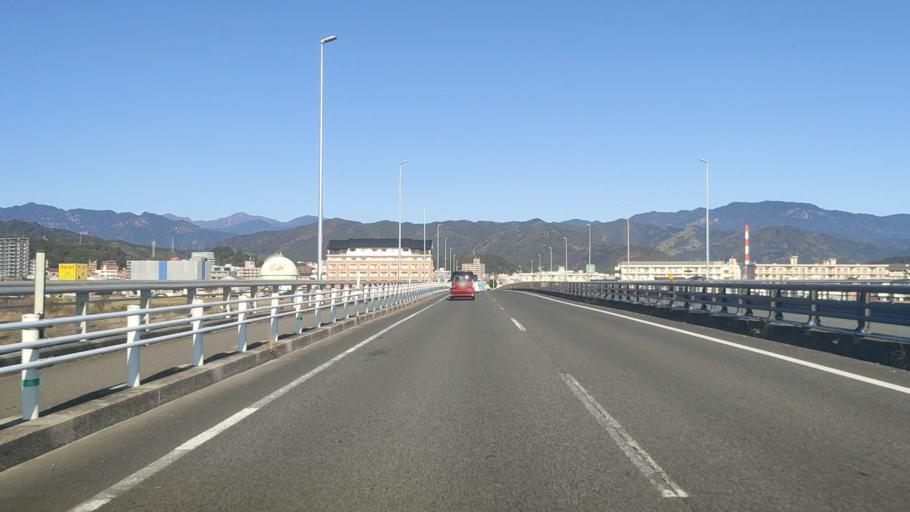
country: JP
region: Miyazaki
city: Nobeoka
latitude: 32.5831
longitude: 131.6798
